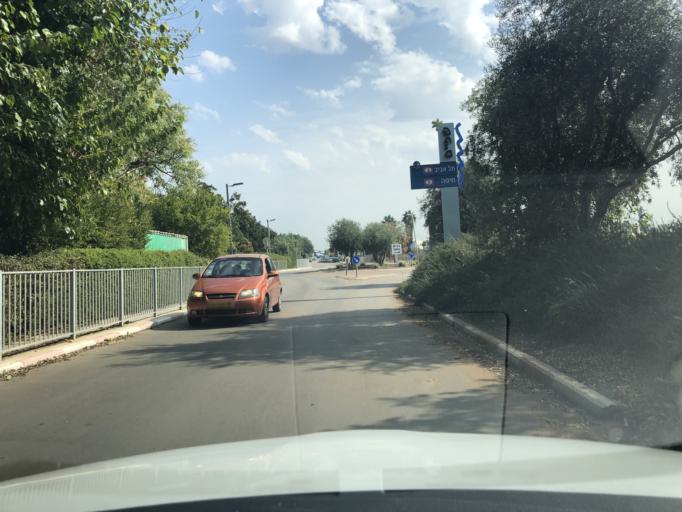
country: IL
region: Tel Aviv
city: Kefar Shemaryahu
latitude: 32.2152
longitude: 34.8226
